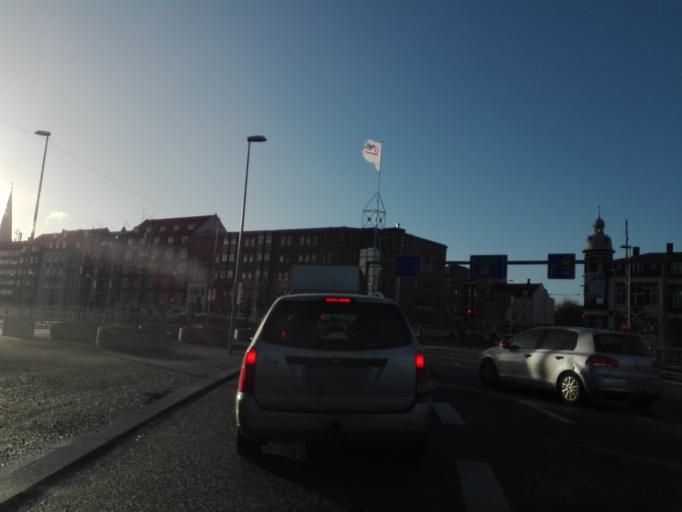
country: DK
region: Central Jutland
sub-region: Arhus Kommune
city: Arhus
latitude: 56.1602
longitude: 10.2157
